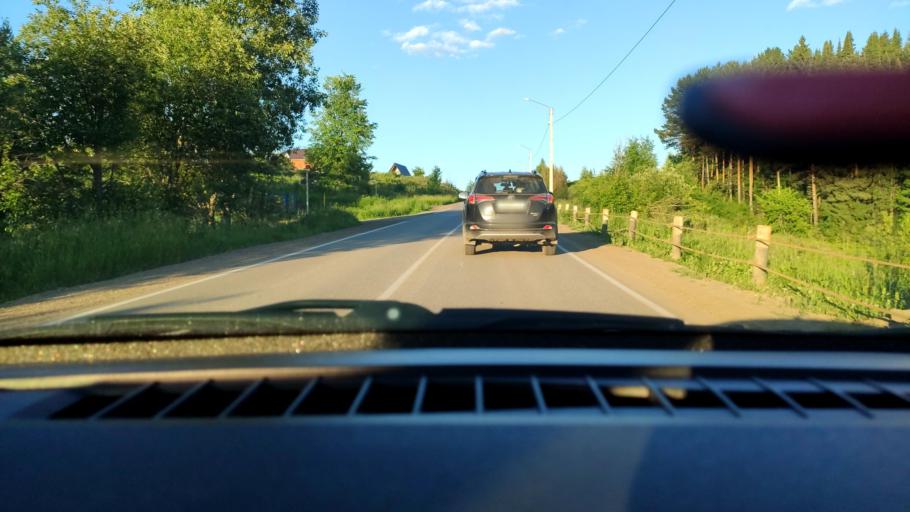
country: RU
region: Perm
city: Kultayevo
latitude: 57.9248
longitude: 55.9003
